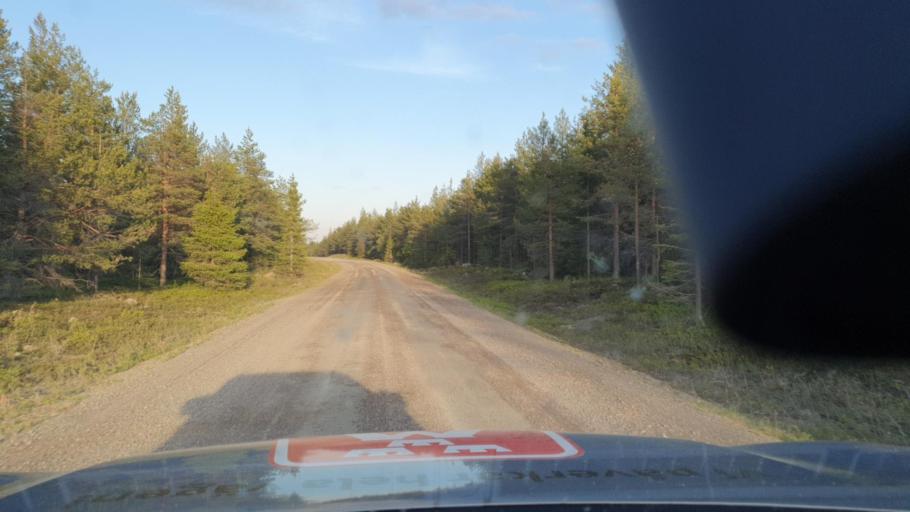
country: SE
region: Norrbotten
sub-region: Bodens Kommun
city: Boden
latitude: 66.4377
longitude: 21.6965
